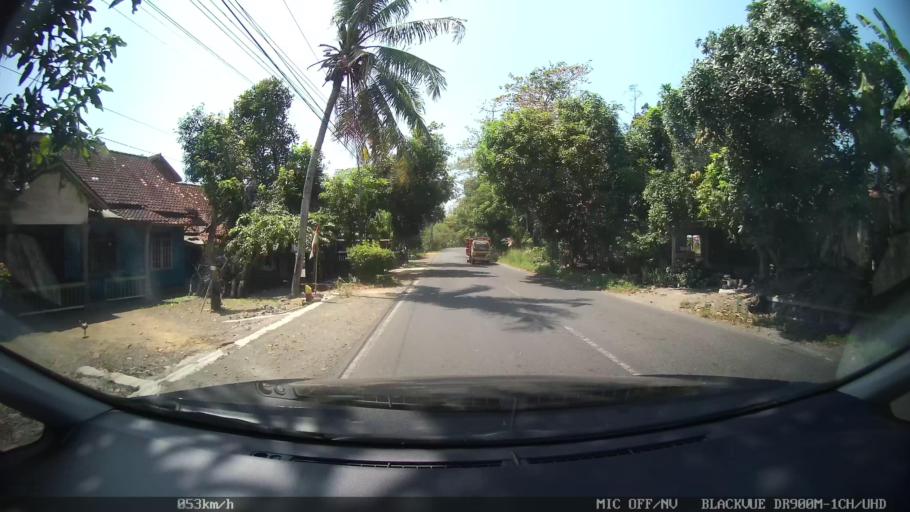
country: ID
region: Daerah Istimewa Yogyakarta
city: Srandakan
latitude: -7.9146
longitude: 110.0972
